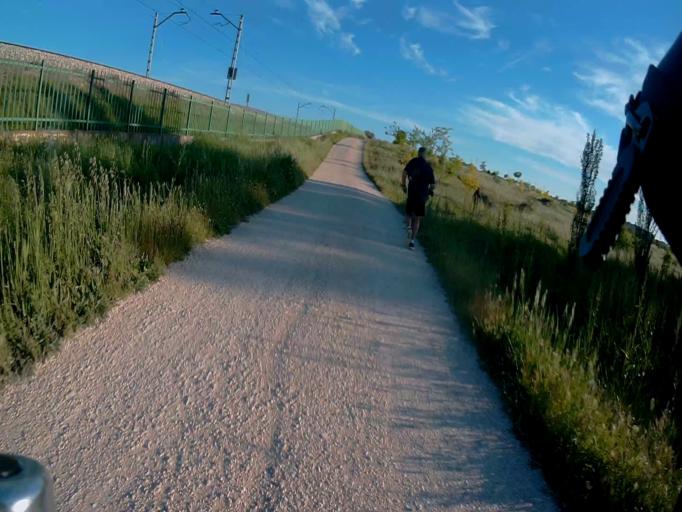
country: ES
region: Madrid
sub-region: Provincia de Madrid
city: Fuenlabrada
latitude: 40.3025
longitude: -3.7894
